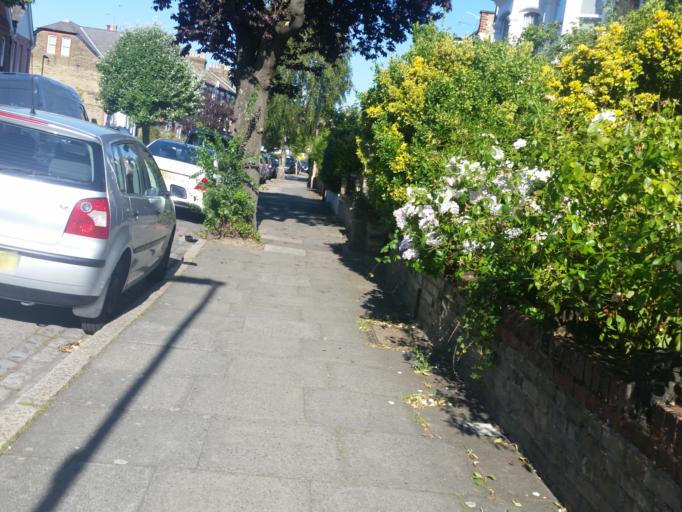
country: GB
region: England
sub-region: Greater London
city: Crouch End
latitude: 51.5832
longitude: -0.1267
